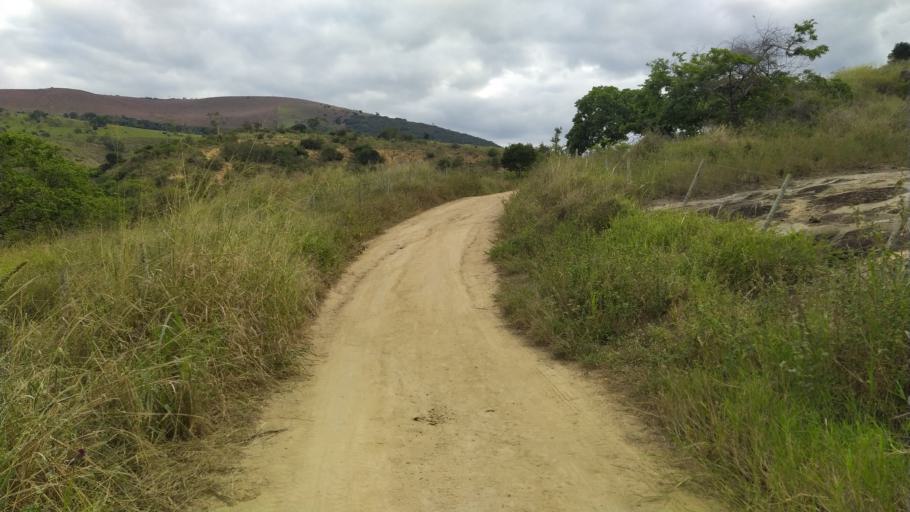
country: BR
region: Minas Gerais
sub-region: Almenara
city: Almenara
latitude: -16.6301
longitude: -40.4600
